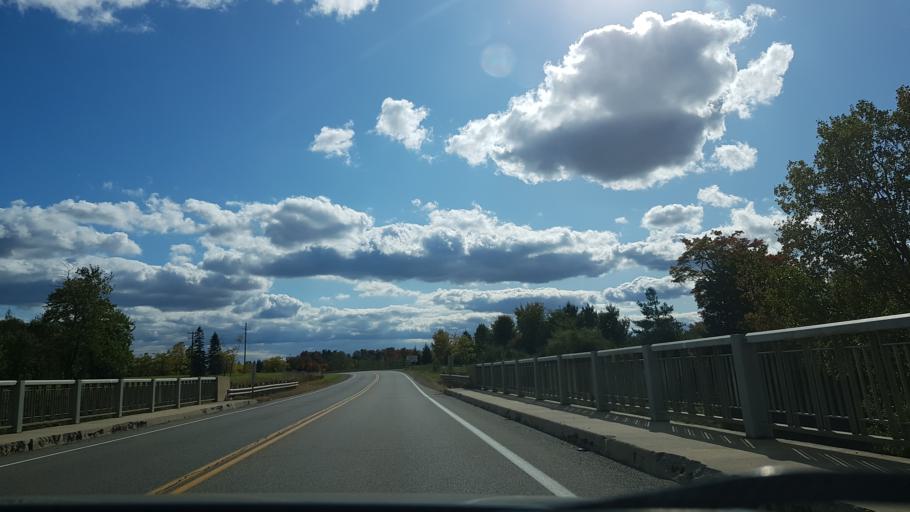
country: CA
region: Ontario
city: South Huron
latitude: 43.1784
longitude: -81.6794
